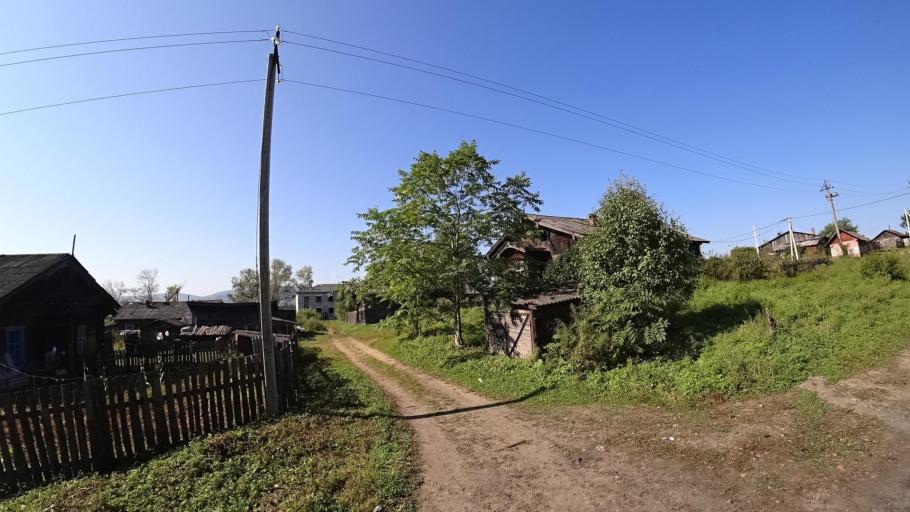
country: RU
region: Jewish Autonomous Oblast
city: Bira
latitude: 49.0023
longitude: 132.4625
